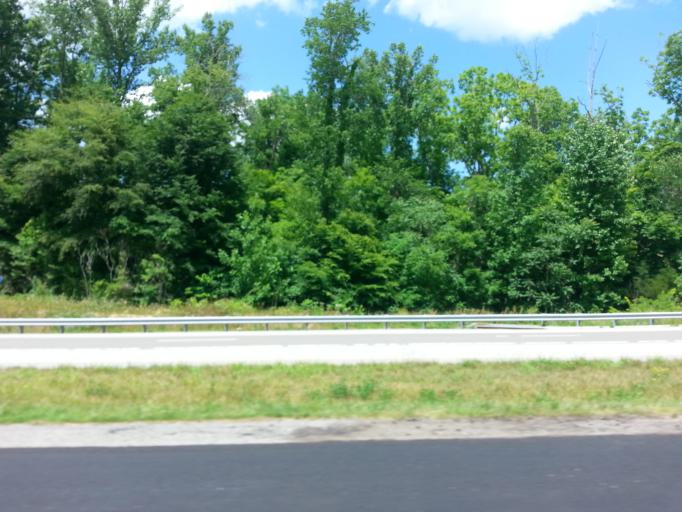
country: US
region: Virginia
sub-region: Lee County
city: Jonesville
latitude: 36.6978
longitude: -83.2525
